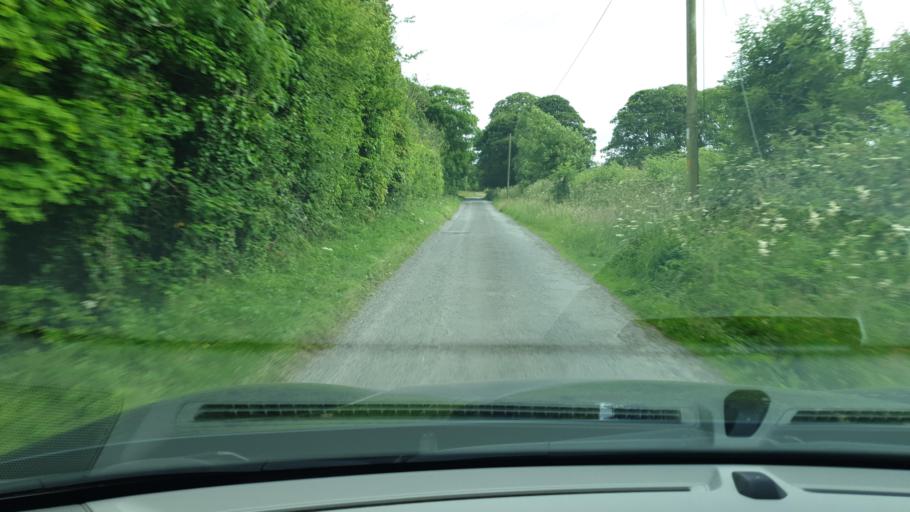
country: IE
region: Leinster
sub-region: An Mhi
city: Dunshaughlin
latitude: 53.5408
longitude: -6.5073
